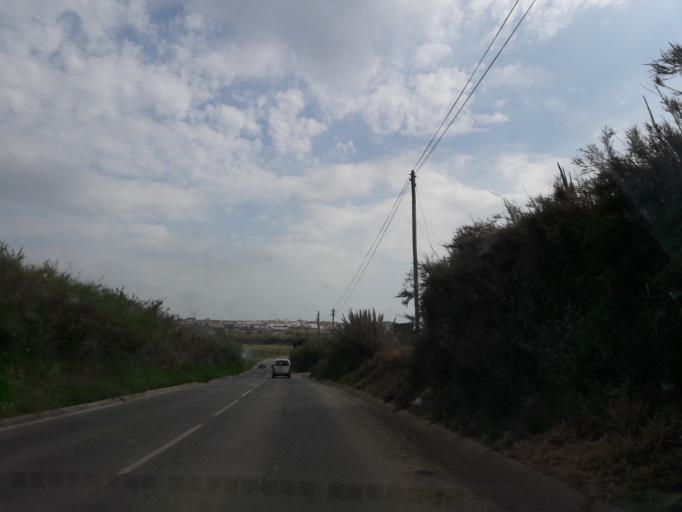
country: PT
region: Leiria
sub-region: Peniche
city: Atouguia da Baleia
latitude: 39.3491
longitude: -9.3238
